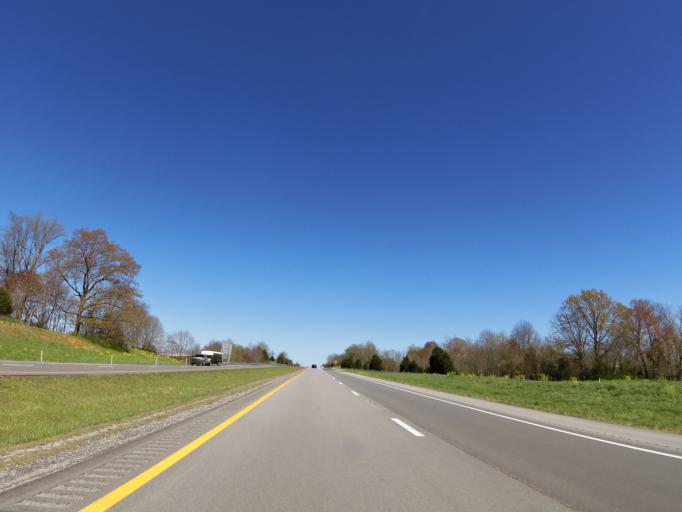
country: US
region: Kentucky
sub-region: Pulaski County
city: Somerset
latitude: 37.0933
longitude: -84.7973
